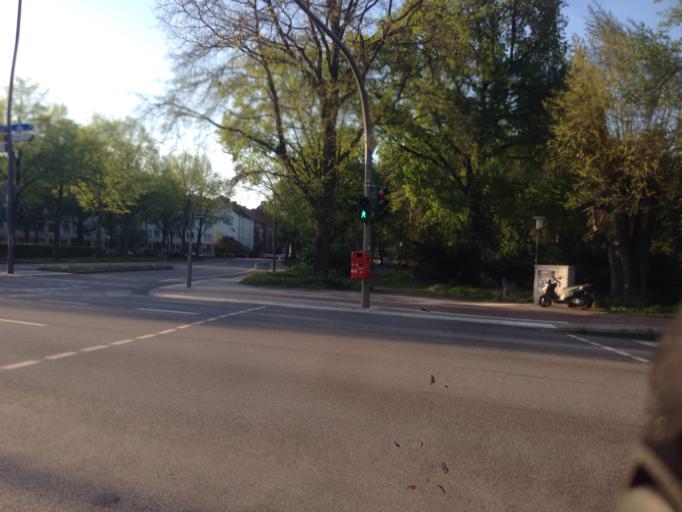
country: DE
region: Hamburg
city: Rothenburgsort
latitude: 53.5509
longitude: 10.0592
